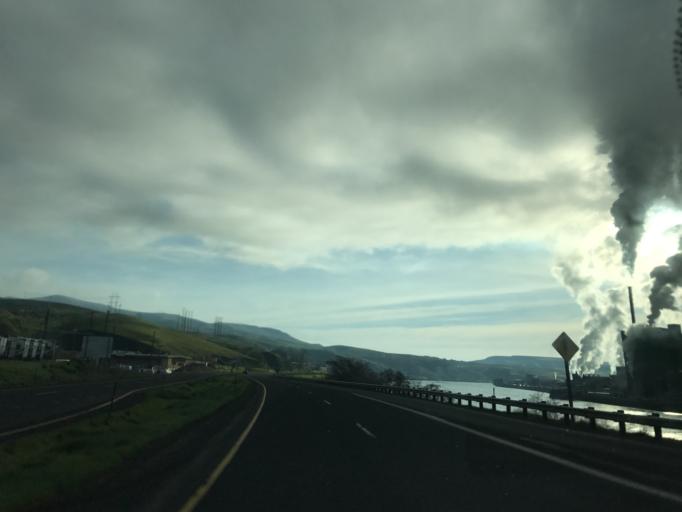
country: US
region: Idaho
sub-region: Nez Perce County
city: Lewiston
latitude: 46.4315
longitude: -116.9822
